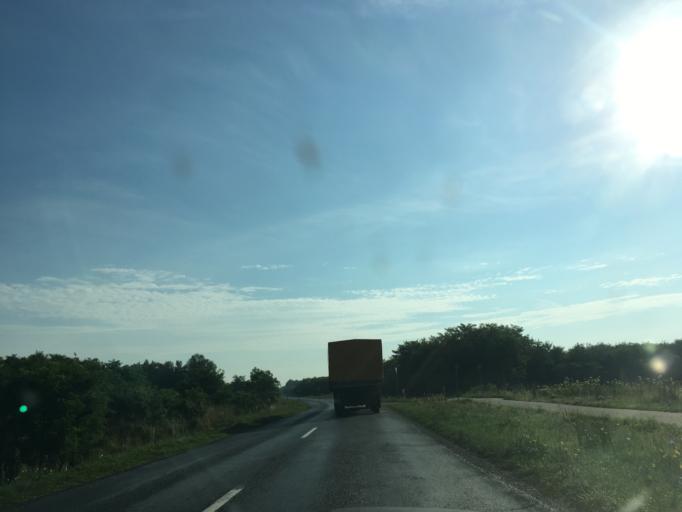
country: HU
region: Hajdu-Bihar
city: Hajdusamson
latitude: 47.6252
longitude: 21.7861
